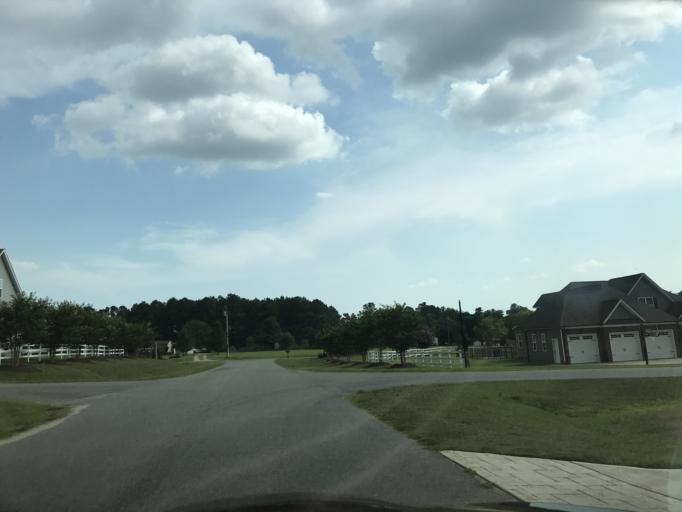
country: US
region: North Carolina
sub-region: Johnston County
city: Four Oaks
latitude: 35.5159
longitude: -78.5316
